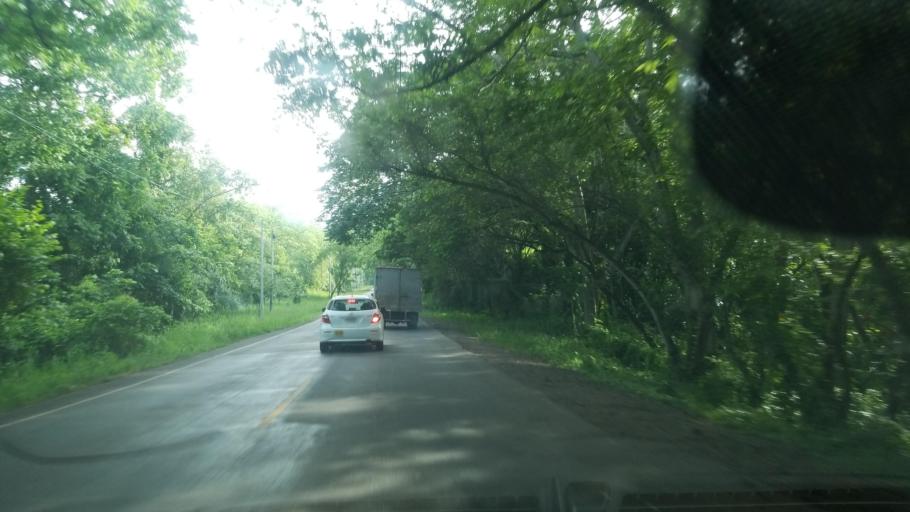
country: HN
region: Santa Barbara
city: Ilama
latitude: 15.0854
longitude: -88.2169
